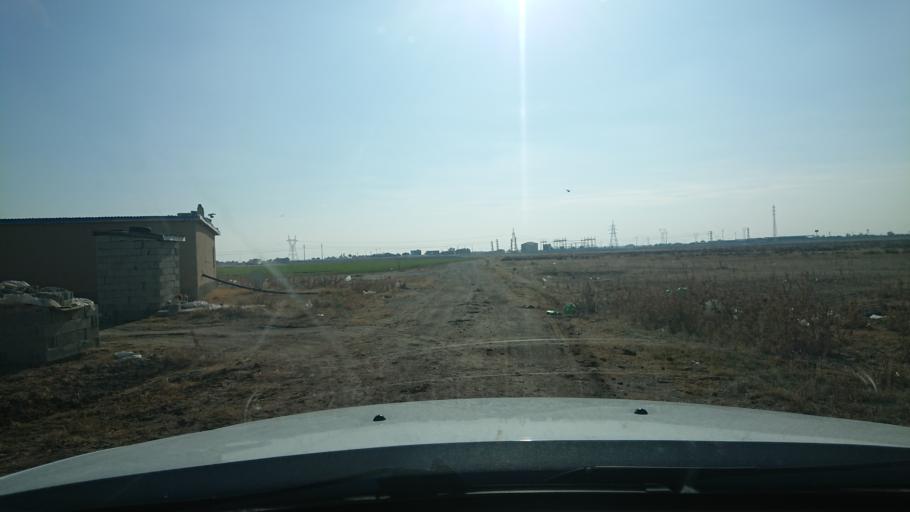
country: TR
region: Aksaray
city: Sultanhani
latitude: 38.2589
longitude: 33.4718
